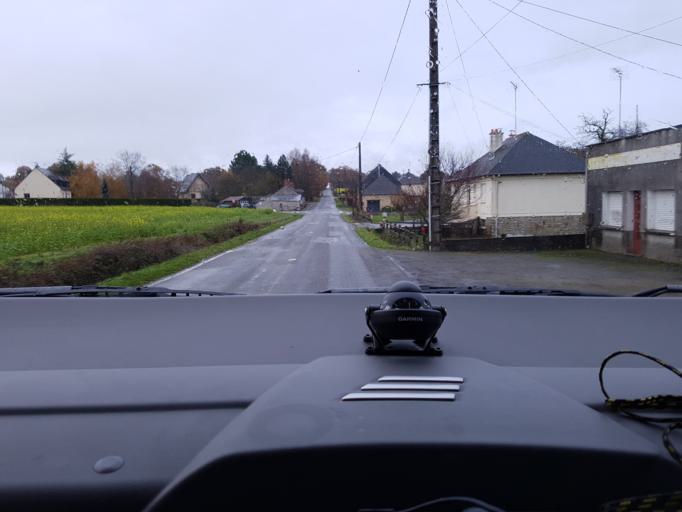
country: FR
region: Brittany
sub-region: Departement d'Ille-et-Vilaine
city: Vitre
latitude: 48.1307
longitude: -1.1630
